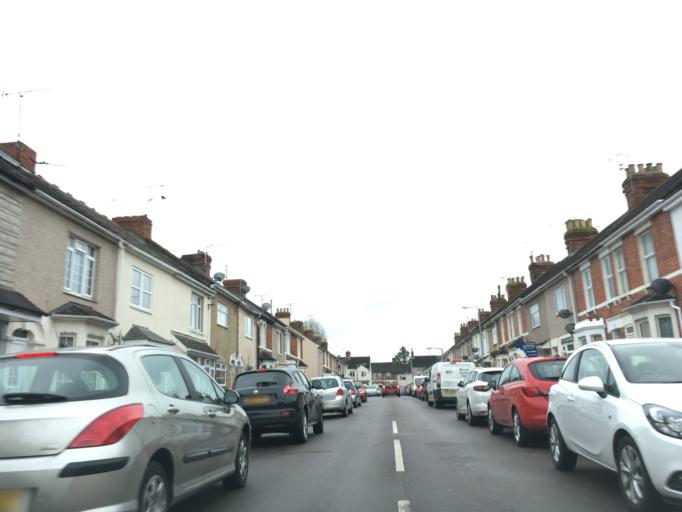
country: GB
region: England
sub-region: Borough of Swindon
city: Swindon
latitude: 51.5647
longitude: -1.8033
